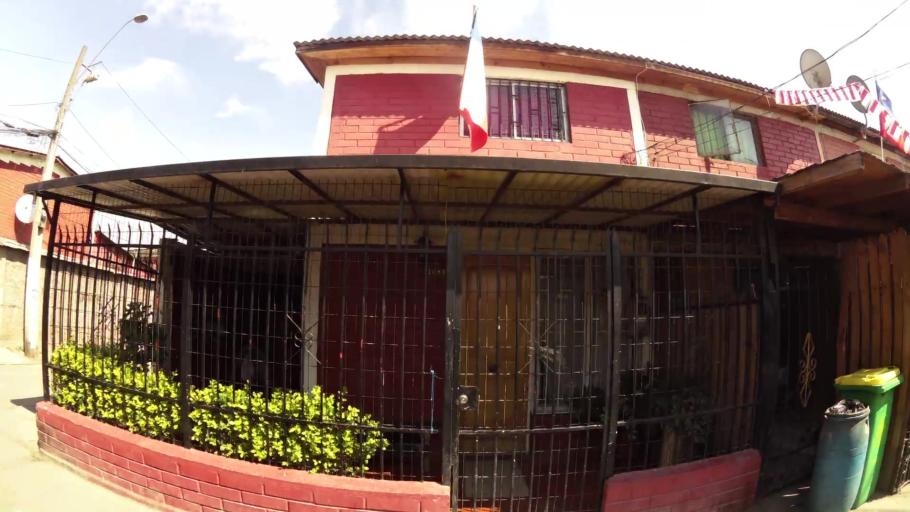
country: CL
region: Santiago Metropolitan
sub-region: Provincia de Santiago
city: La Pintana
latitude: -33.5593
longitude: -70.6513
